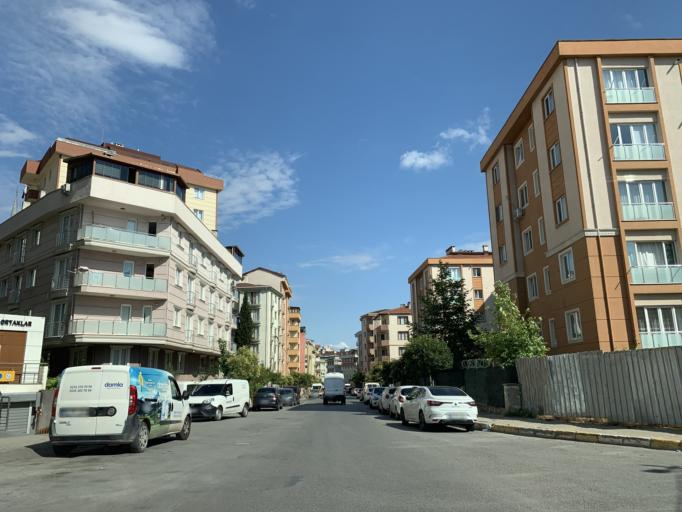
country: TR
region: Istanbul
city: Pendik
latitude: 40.8884
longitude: 29.2663
